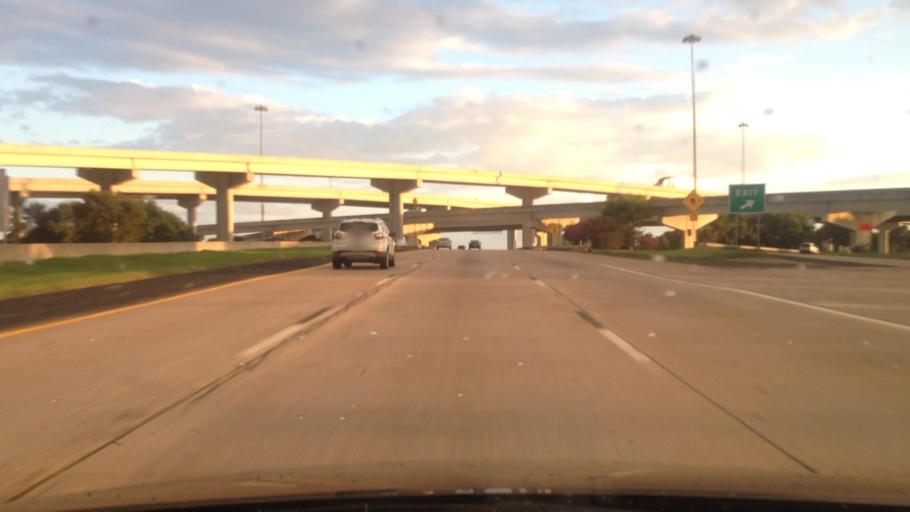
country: US
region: Texas
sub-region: Tarrant County
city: White Settlement
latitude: 32.7402
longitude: -97.4815
